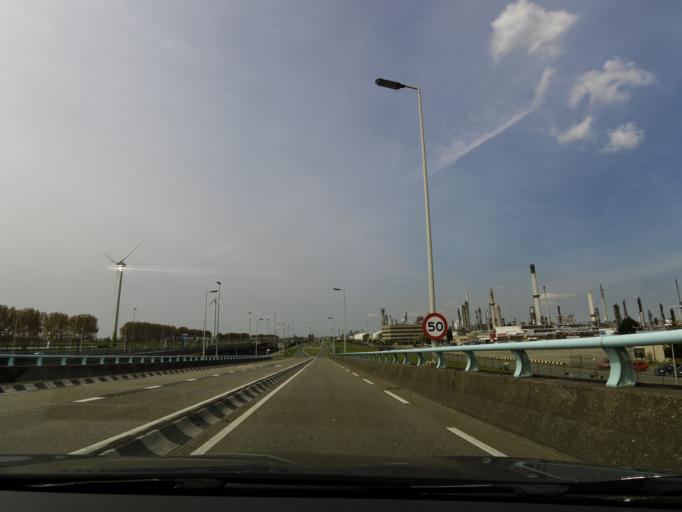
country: NL
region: South Holland
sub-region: Gemeente Spijkenisse
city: Spijkenisse
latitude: 51.8696
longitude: 4.3057
